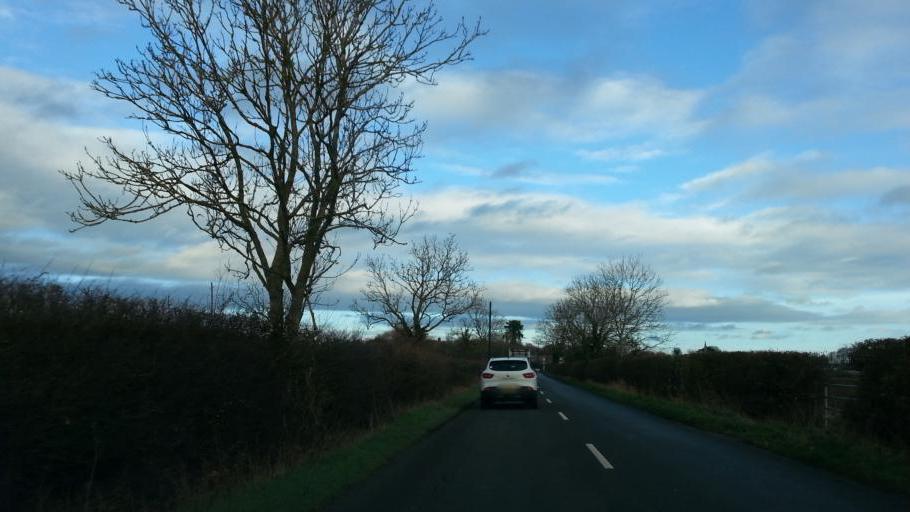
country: GB
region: England
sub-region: Oxfordshire
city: Faringdon
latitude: 51.6364
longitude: -1.5504
